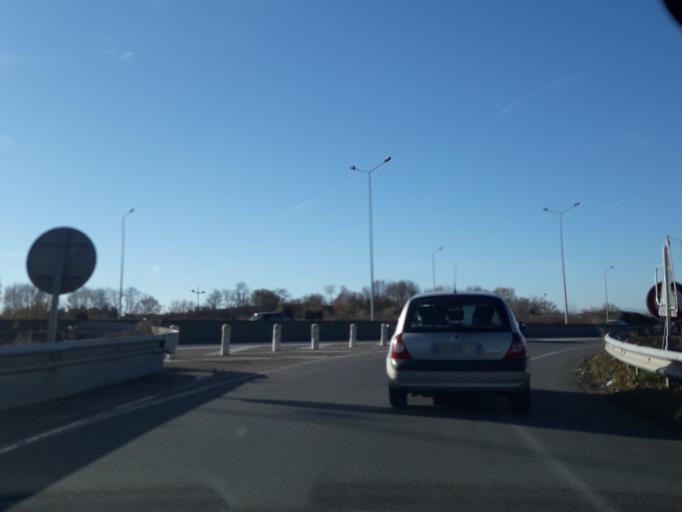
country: FR
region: Rhone-Alpes
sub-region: Departement du Rhone
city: Saint-Priest
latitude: 45.7029
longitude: 4.9675
